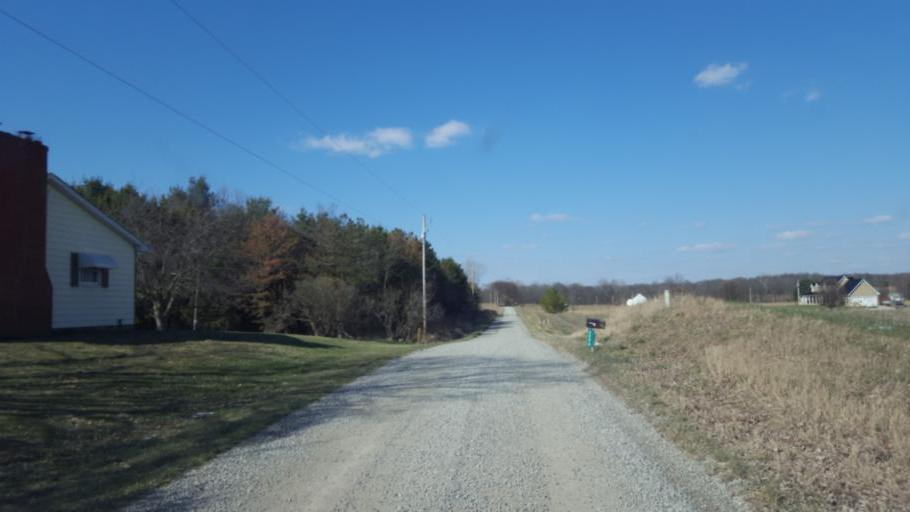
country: US
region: Ohio
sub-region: Morrow County
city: Mount Gilead
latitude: 40.4703
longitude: -82.7445
